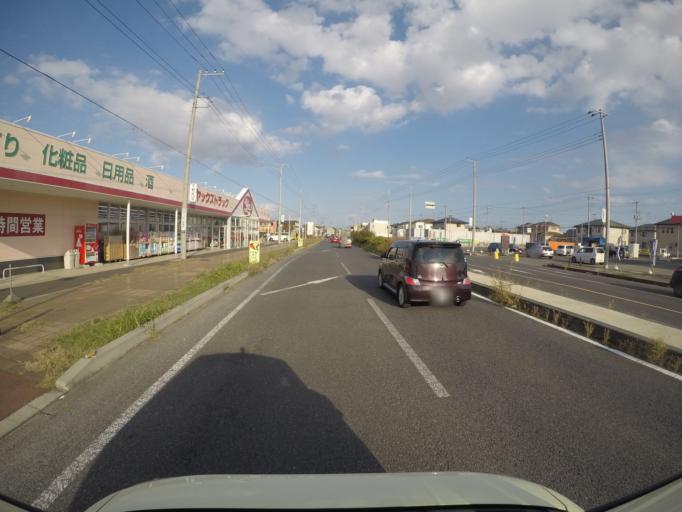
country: JP
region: Ibaraki
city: Mitsukaido
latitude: 35.9995
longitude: 140.0417
